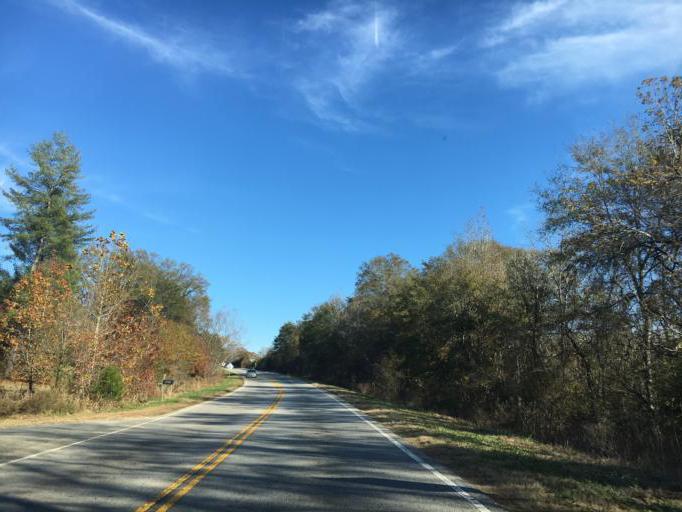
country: US
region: South Carolina
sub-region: Spartanburg County
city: Wellford
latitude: 34.9597
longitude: -82.0760
